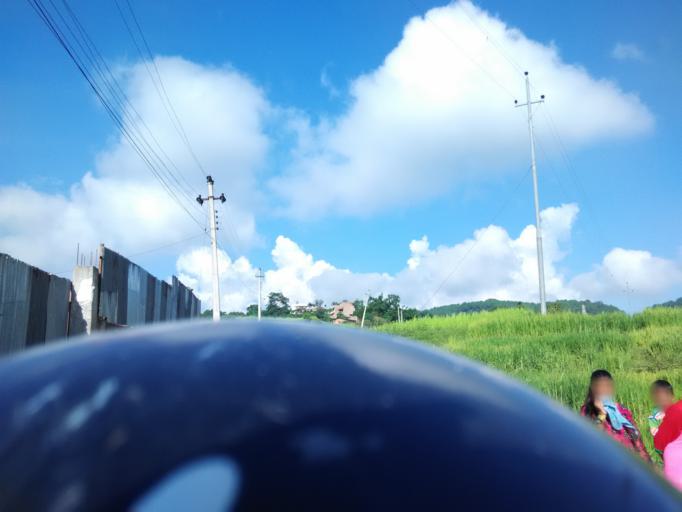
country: NP
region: Central Region
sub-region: Bagmati Zone
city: Patan
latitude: 27.6066
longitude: 85.3480
